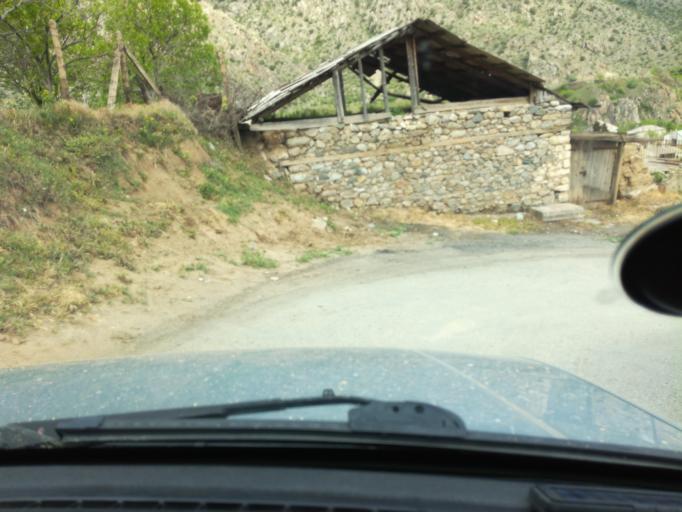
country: AM
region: Syunik'i Marz
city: Meghri
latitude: 38.9399
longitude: 46.2155
